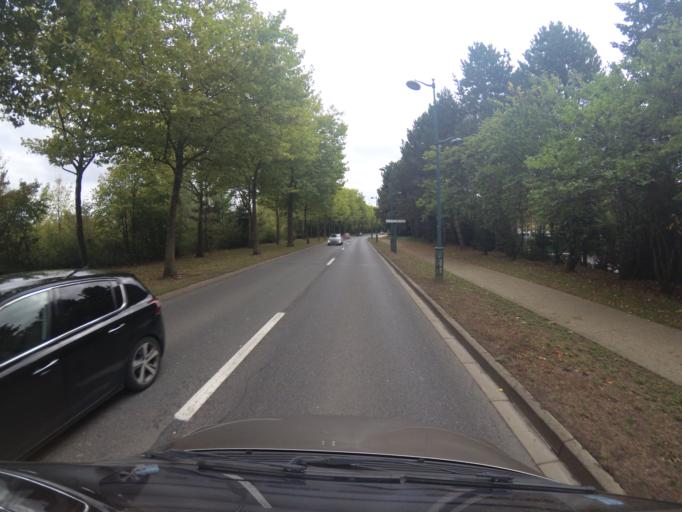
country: FR
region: Ile-de-France
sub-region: Departement de Seine-et-Marne
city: Serris
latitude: 48.8655
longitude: 2.7915
